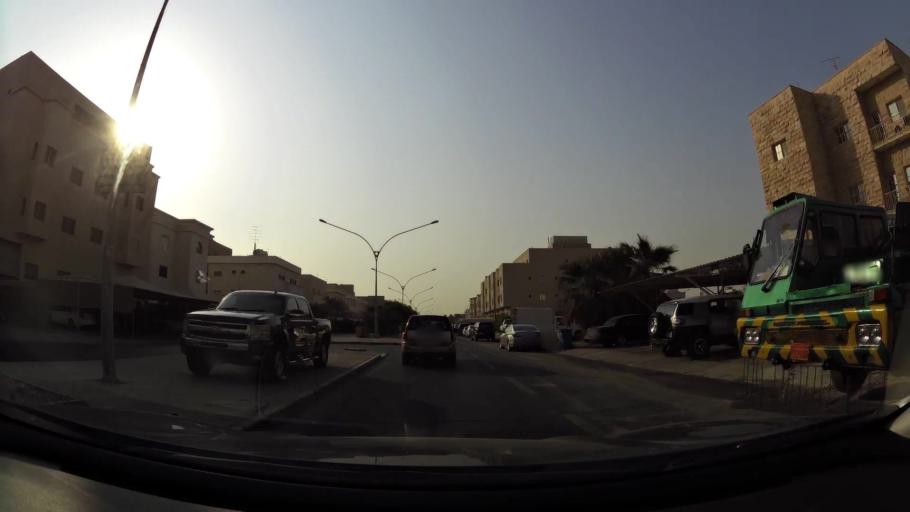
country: KW
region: Muhafazat Hawalli
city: Salwa
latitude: 29.3008
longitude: 48.0731
